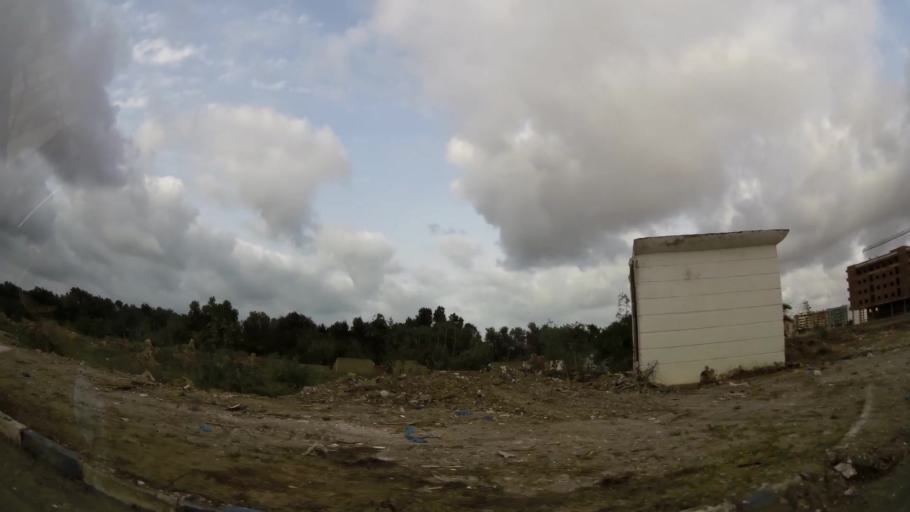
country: MA
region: Oriental
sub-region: Nador
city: Nador
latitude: 35.1557
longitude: -2.9206
